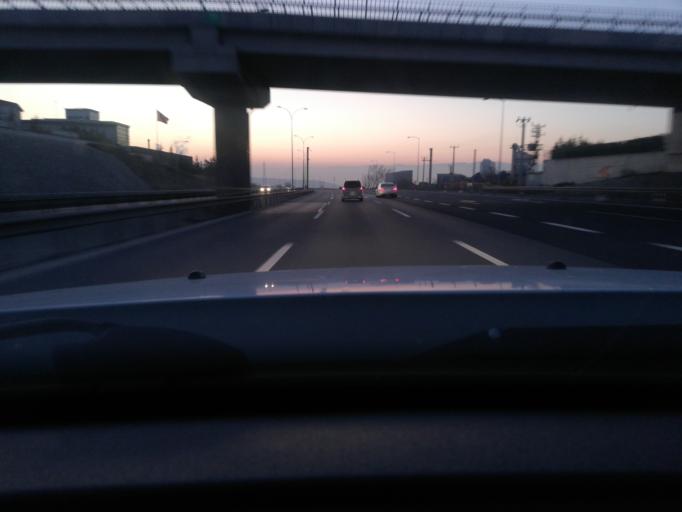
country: TR
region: Kocaeli
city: Tavsanli
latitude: 40.8024
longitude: 29.4995
